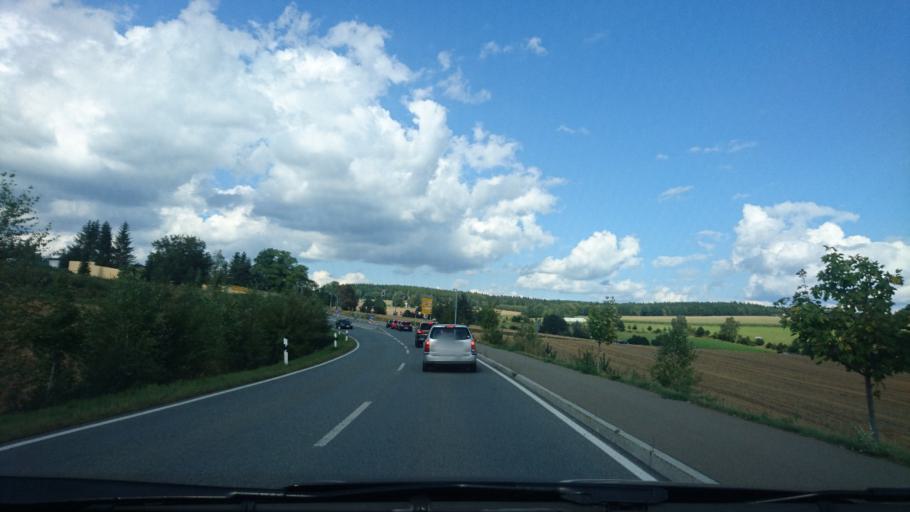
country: DE
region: Saxony
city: Treuen
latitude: 50.5452
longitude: 12.3138
